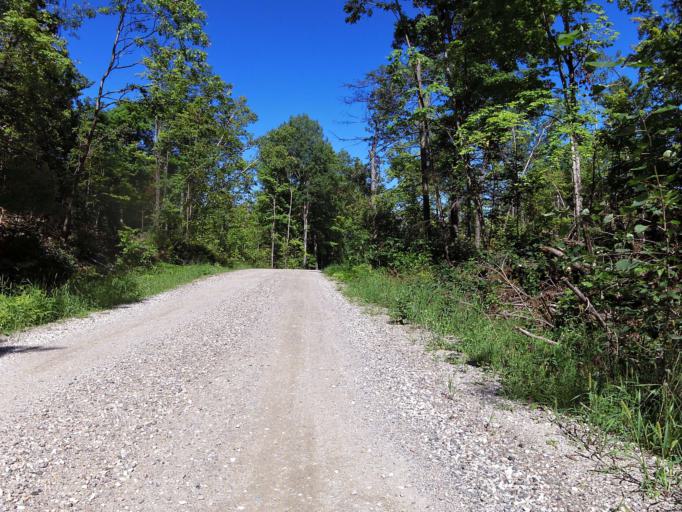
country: CA
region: Ontario
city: Renfrew
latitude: 45.1340
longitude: -76.7079
